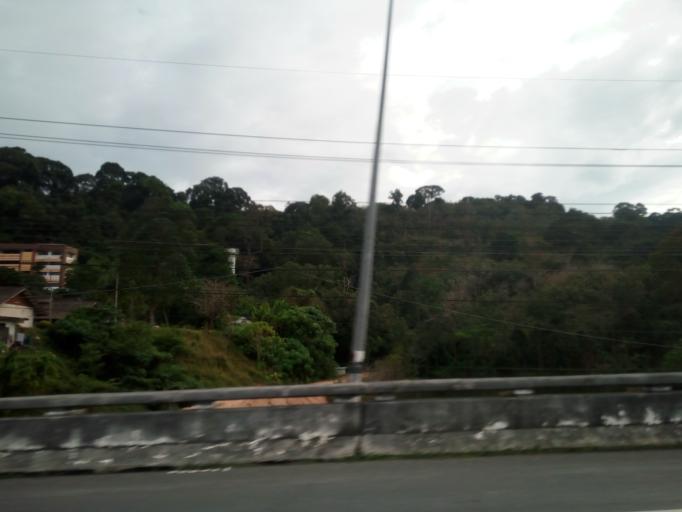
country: TH
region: Phuket
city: Thalang
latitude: 8.0896
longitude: 98.3221
